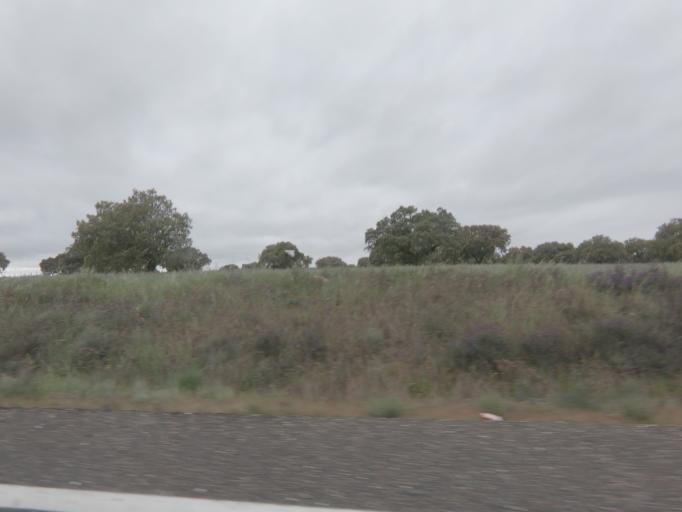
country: ES
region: Extremadura
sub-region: Provincia de Badajoz
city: La Roca de la Sierra
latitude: 39.0670
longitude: -6.7607
